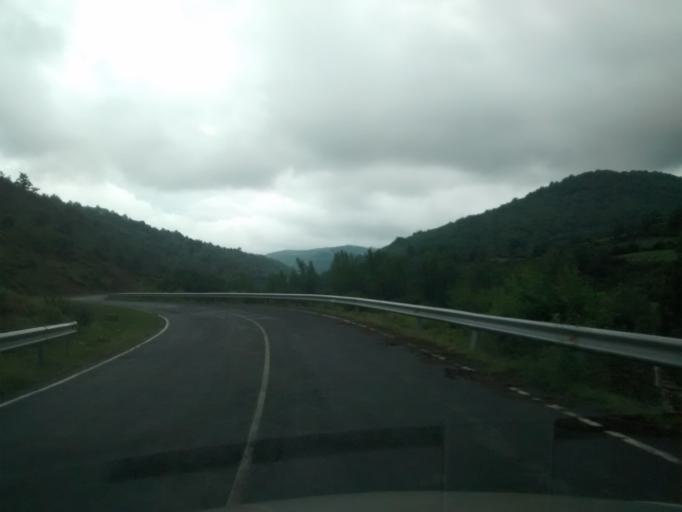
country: ES
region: La Rioja
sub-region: Provincia de La Rioja
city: Rabanera
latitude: 42.1860
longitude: -2.4839
